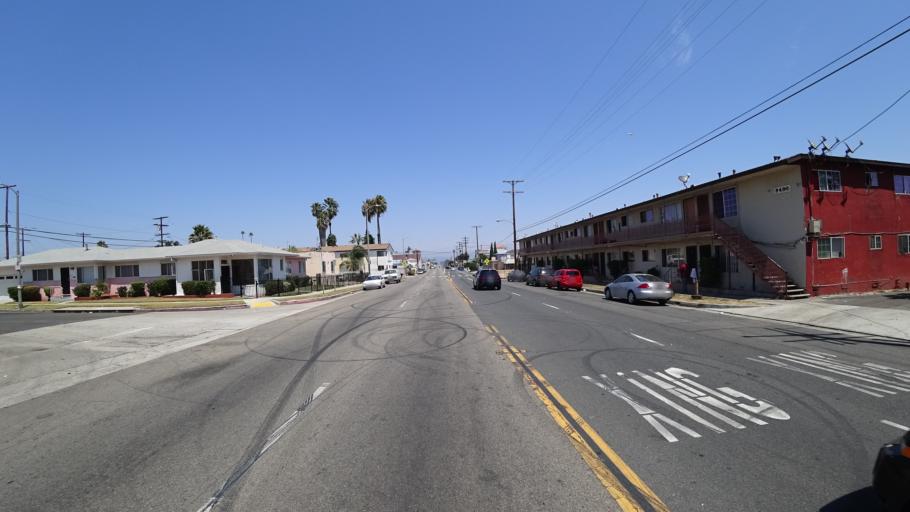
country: US
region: California
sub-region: Los Angeles County
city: Westmont
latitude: 33.9503
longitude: -118.3003
